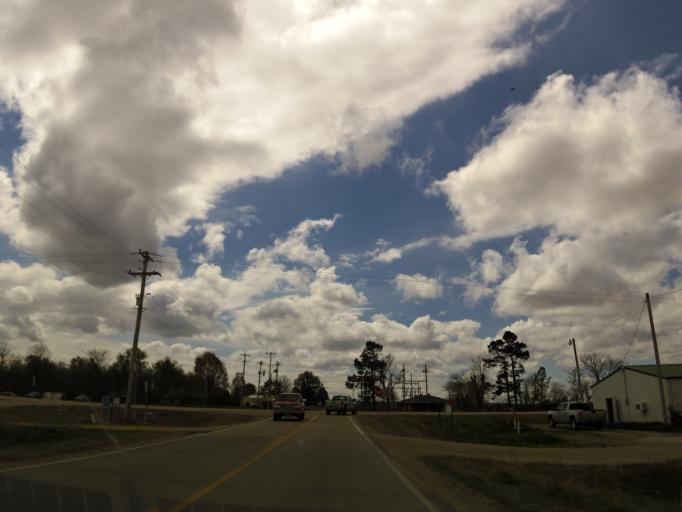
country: US
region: Arkansas
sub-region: Greene County
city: Paragould
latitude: 36.0696
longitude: -90.6725
